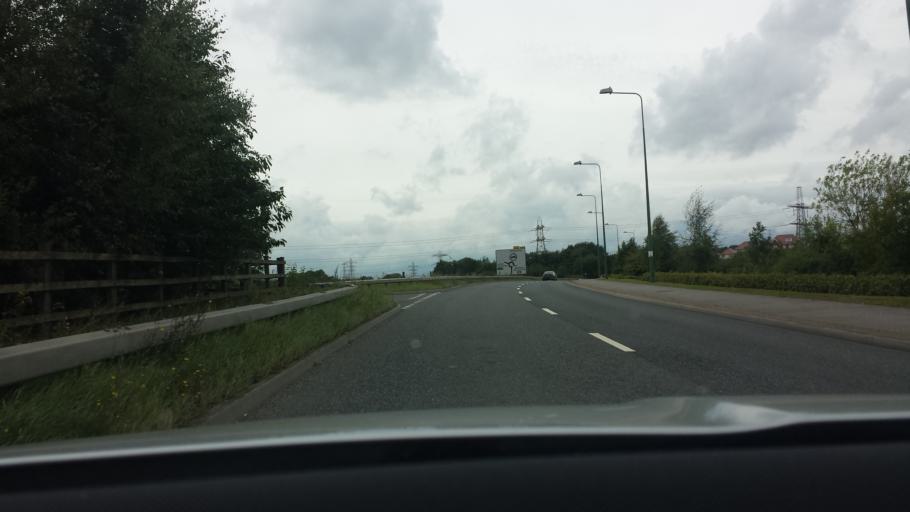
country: GB
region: England
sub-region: Kent
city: Swanscombe
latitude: 51.4366
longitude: 0.3214
